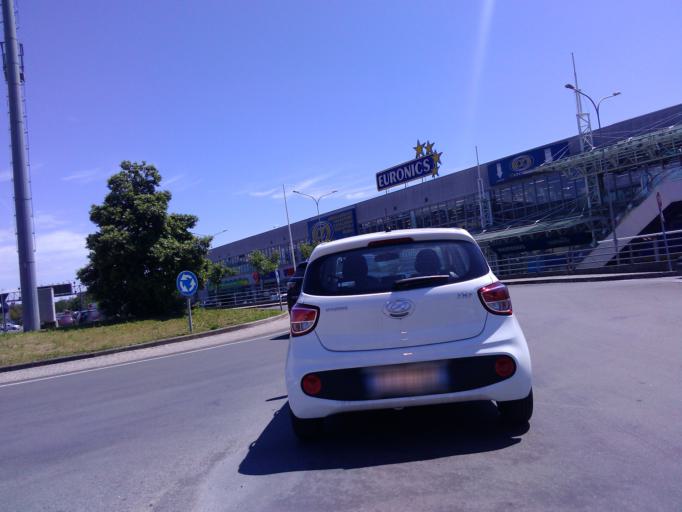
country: IT
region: Liguria
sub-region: Provincia di La Spezia
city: Sarzana
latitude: 44.1176
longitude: 9.9451
